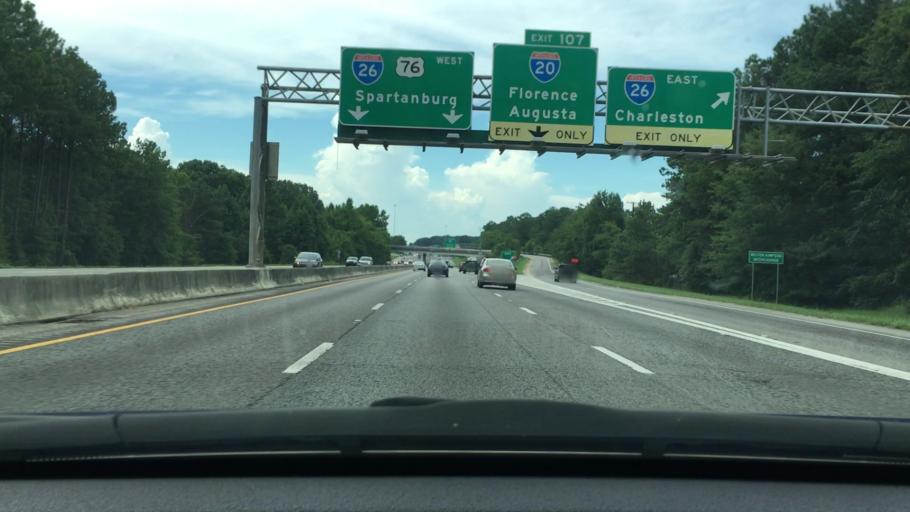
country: US
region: South Carolina
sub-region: Lexington County
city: West Columbia
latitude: 34.0224
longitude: -81.0962
